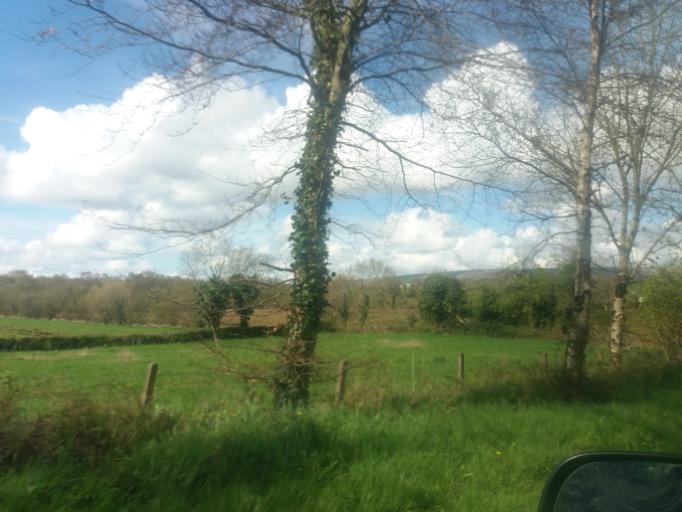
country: IE
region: Ulster
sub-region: An Cabhan
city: Belturbet
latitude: 54.1398
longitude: -7.5083
